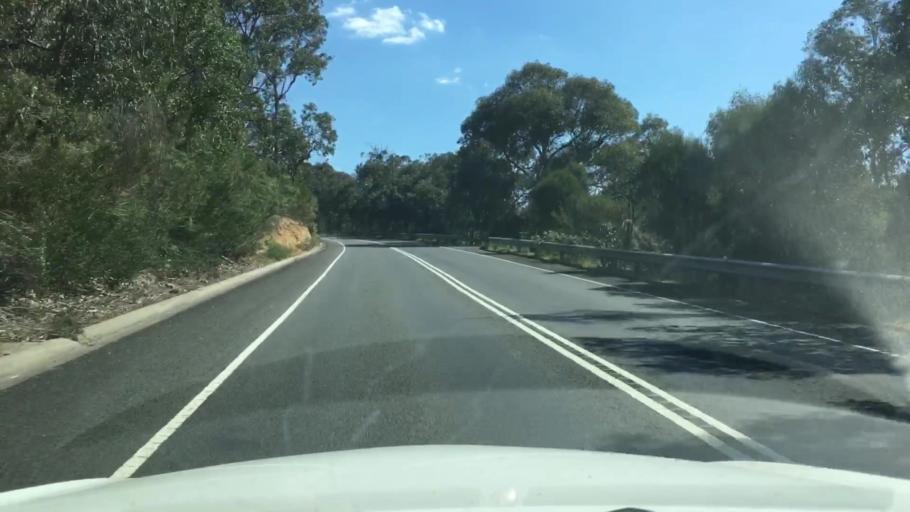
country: AU
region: Victoria
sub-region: Nillumbik
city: North Warrandyte
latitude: -37.6767
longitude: 145.2450
